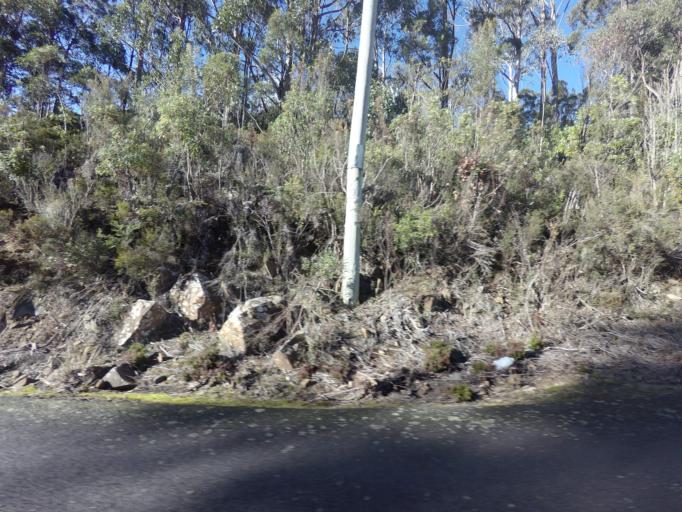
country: AU
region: Tasmania
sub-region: Glenorchy
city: Berriedale
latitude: -42.8391
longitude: 147.1652
